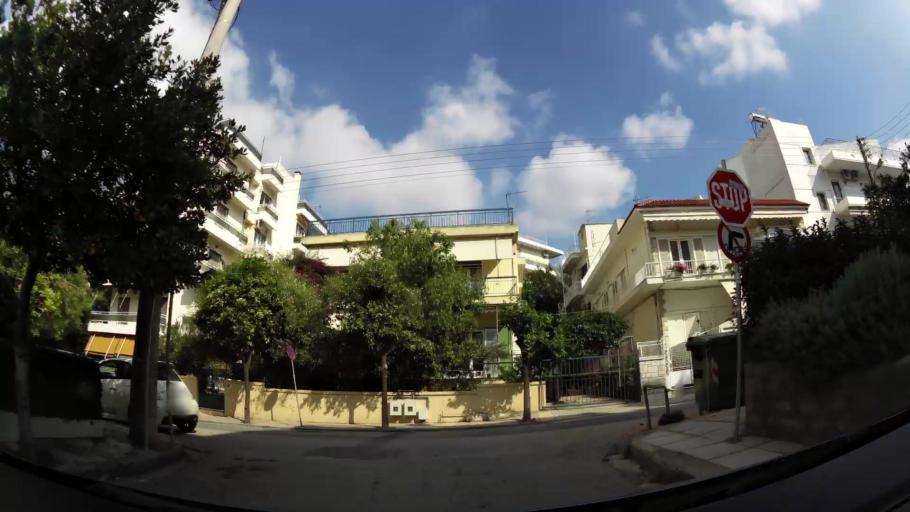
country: GR
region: Attica
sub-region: Nomarchia Athinas
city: Cholargos
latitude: 37.9954
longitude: 23.7997
